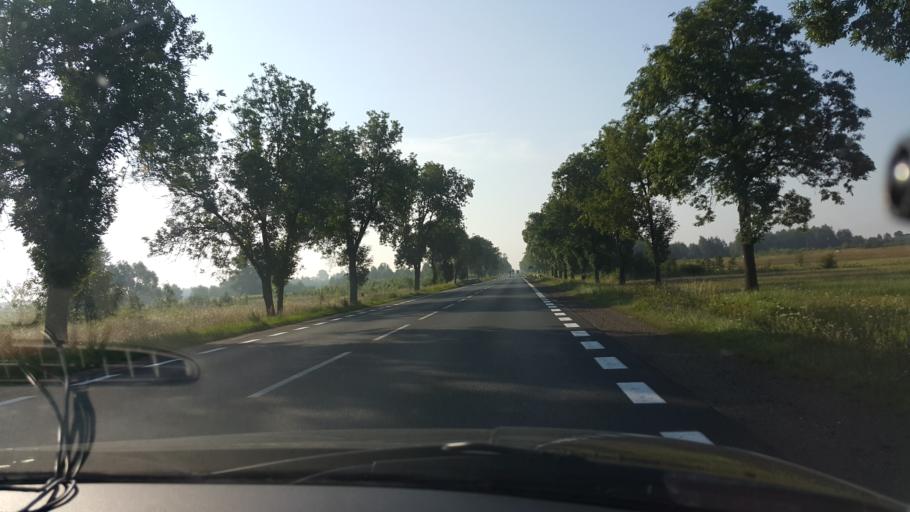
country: PL
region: Masovian Voivodeship
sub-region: Powiat radomski
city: Jedlnia-Letnisko
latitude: 51.4000
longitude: 21.2569
